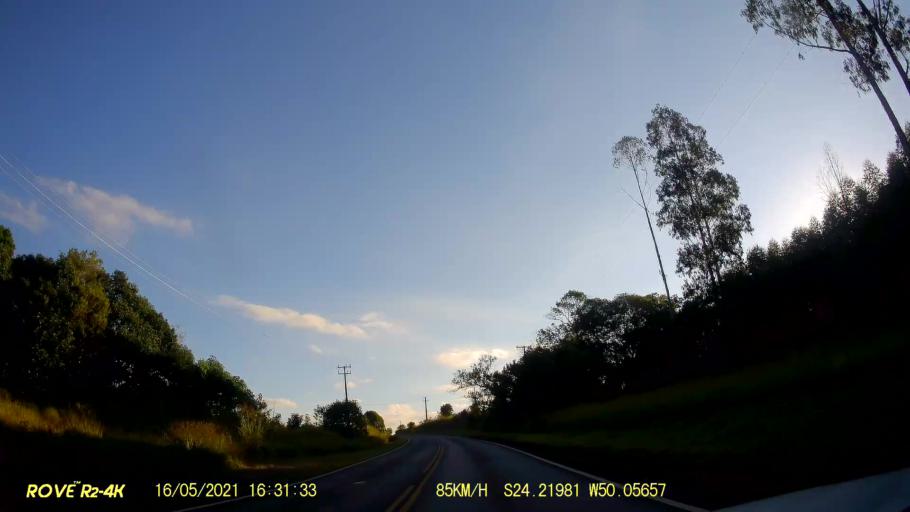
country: BR
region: Parana
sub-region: Pirai Do Sul
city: Pirai do Sul
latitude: -24.2199
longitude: -50.0569
